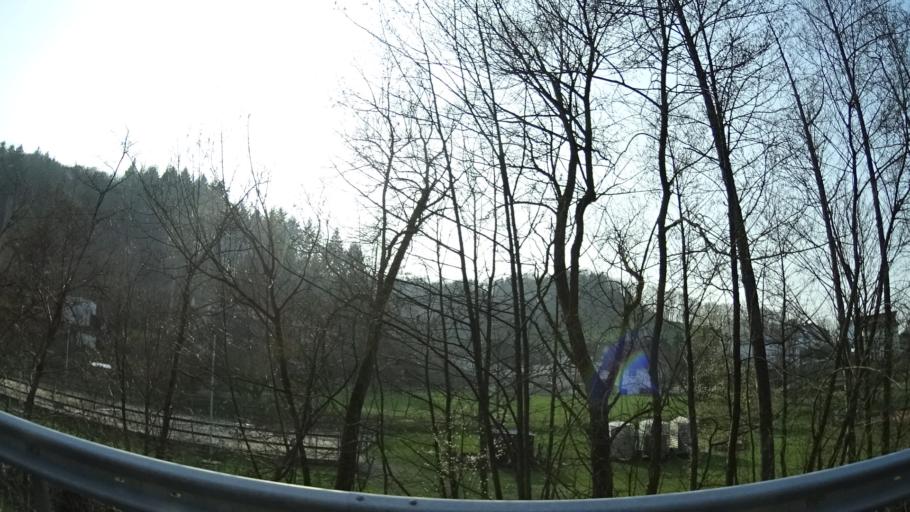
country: DE
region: Rheinland-Pfalz
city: Fockelberg
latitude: 49.5415
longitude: 7.4972
